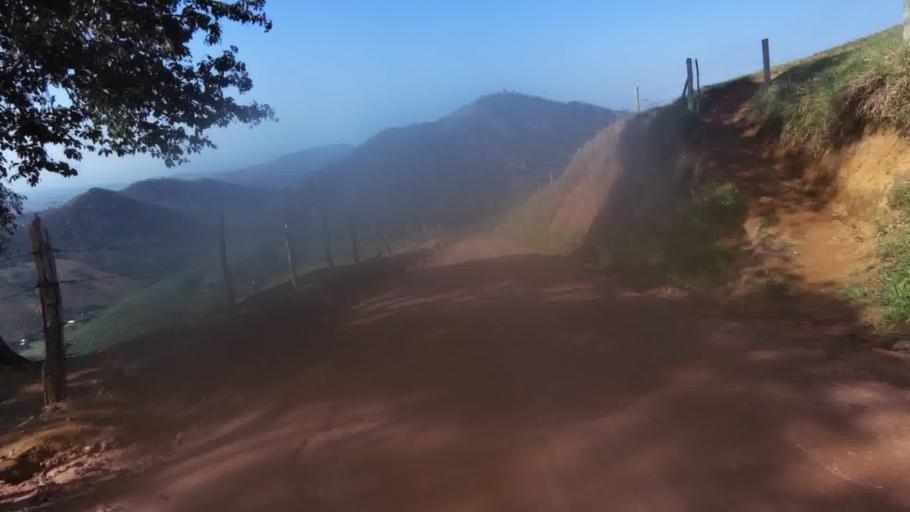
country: BR
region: Espirito Santo
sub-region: Alfredo Chaves
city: Alfredo Chaves
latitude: -20.6801
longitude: -40.7819
